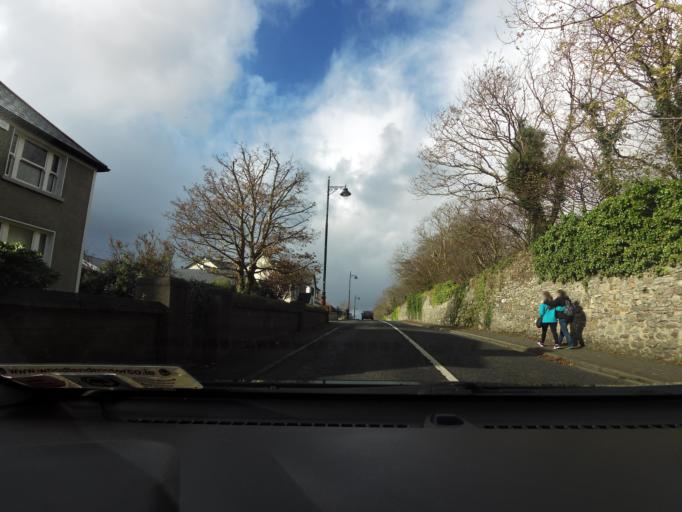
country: IE
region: Connaught
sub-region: Maigh Eo
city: Westport
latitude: 53.7979
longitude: -9.5329
